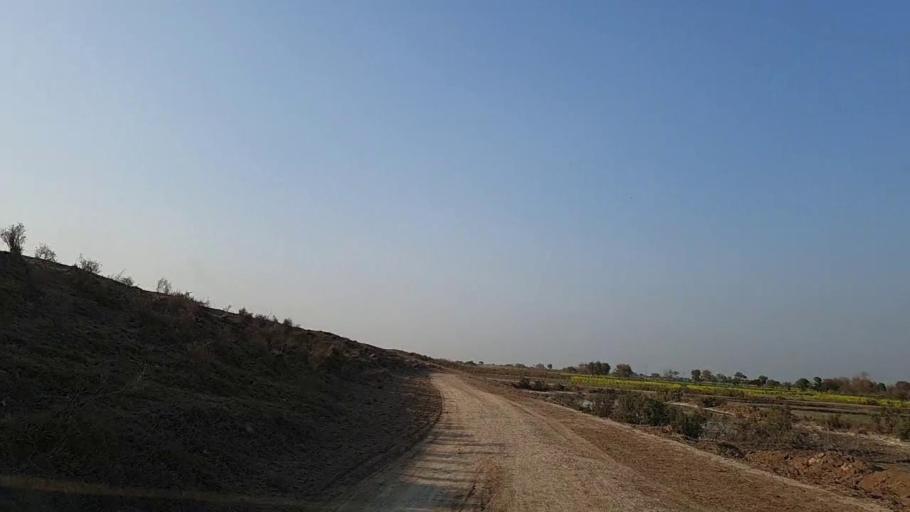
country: PK
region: Sindh
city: Sakrand
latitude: 26.1023
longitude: 68.3659
